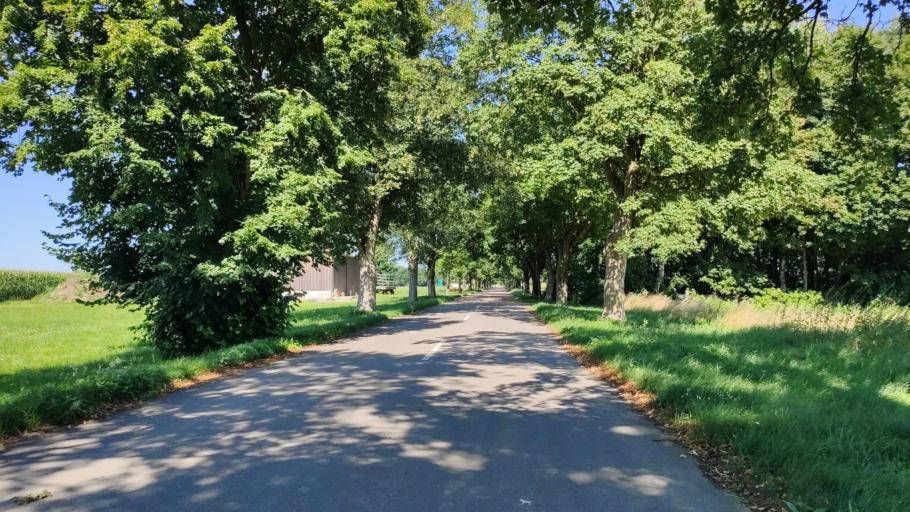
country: DE
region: Bavaria
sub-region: Swabia
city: Kleinaitingen
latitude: 48.2114
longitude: 10.8528
